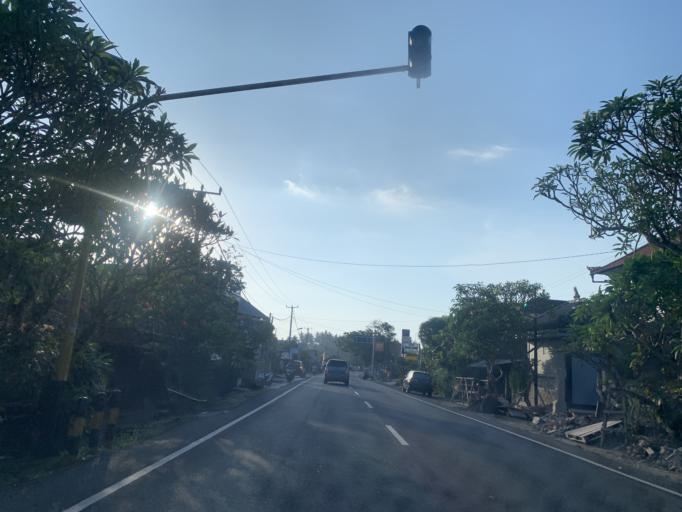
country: ID
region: Bali
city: Banjar Delodrurung
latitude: -8.4947
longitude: 114.9646
